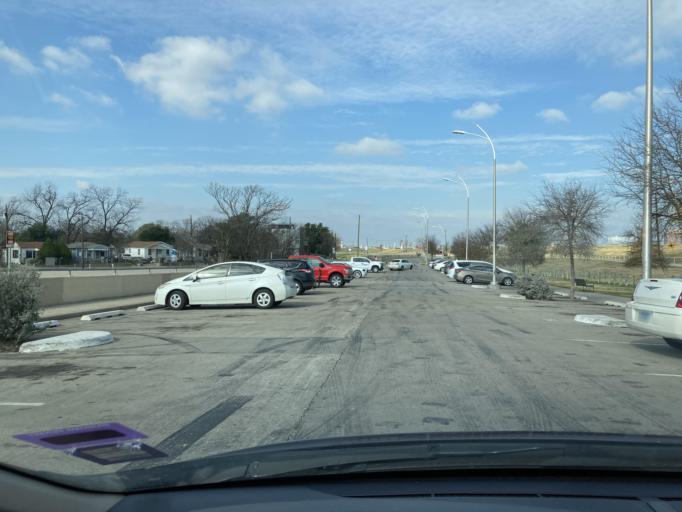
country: US
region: Texas
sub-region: Dallas County
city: Dallas
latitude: 32.7799
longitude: -96.8268
